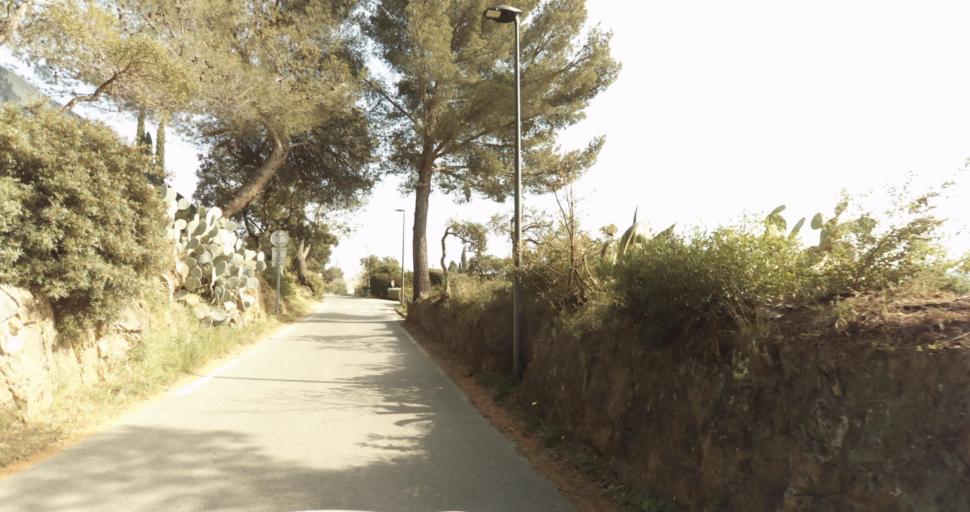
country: FR
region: Provence-Alpes-Cote d'Azur
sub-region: Departement du Var
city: Bormes-les-Mimosas
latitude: 43.1453
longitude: 6.3270
